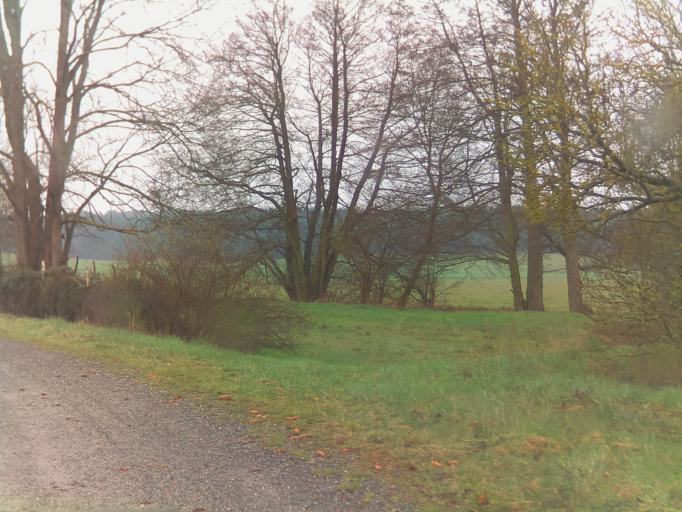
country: DE
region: Brandenburg
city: Friedland
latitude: 52.0365
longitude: 14.2240
